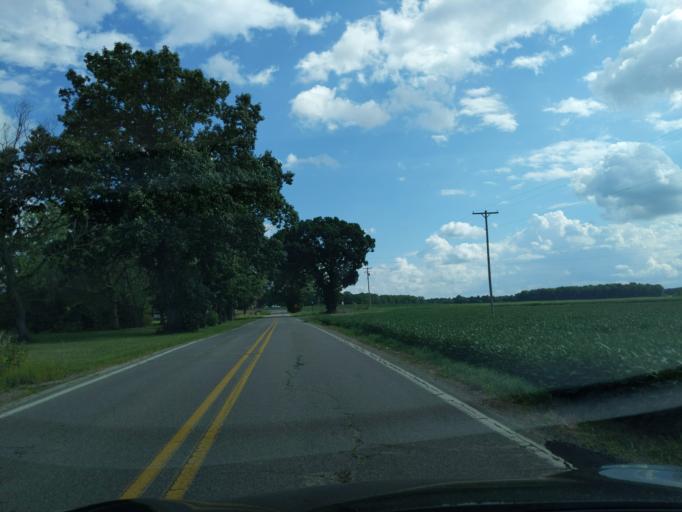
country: US
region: Michigan
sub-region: Jackson County
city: Spring Arbor
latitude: 42.3298
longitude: -84.5413
